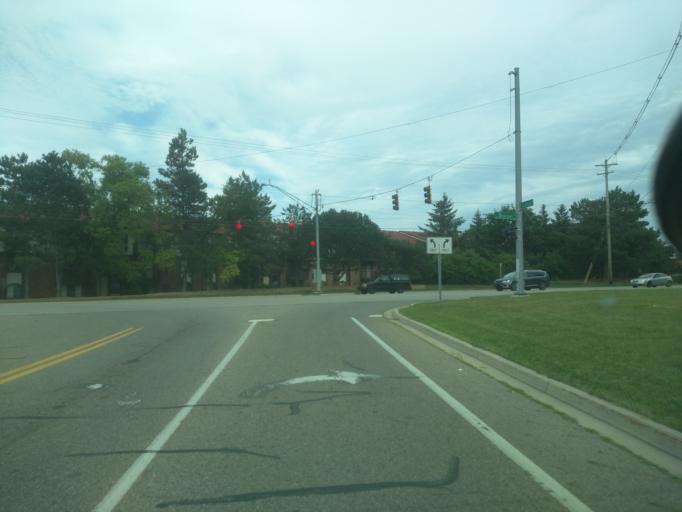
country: US
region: Michigan
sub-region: Ingham County
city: Holt
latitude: 42.6869
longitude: -84.5139
